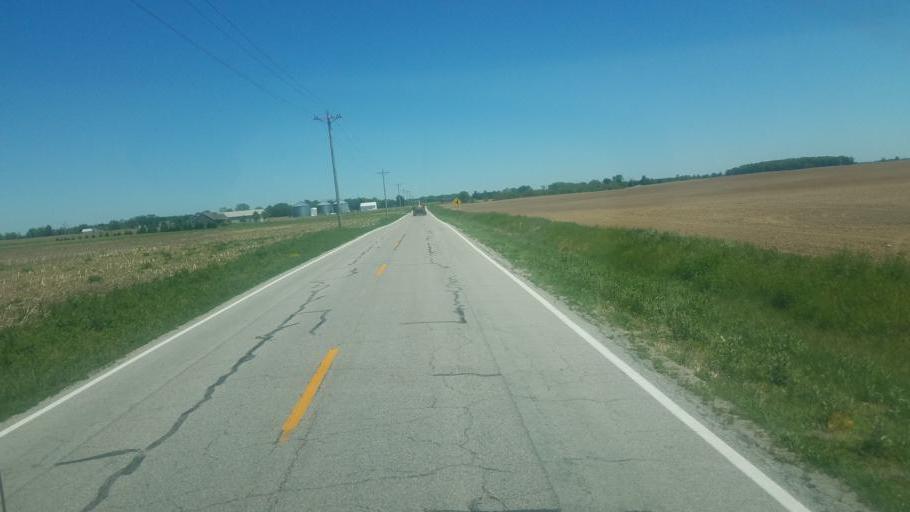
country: US
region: Ohio
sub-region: Miami County
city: Piqua
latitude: 40.2129
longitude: -84.3021
